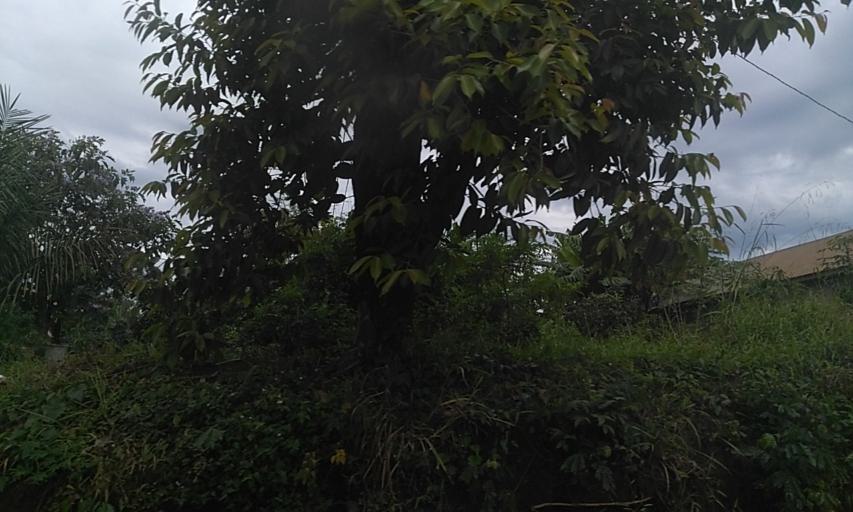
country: UG
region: Central Region
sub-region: Wakiso District
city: Bweyogerere
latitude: 0.3963
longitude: 32.6998
